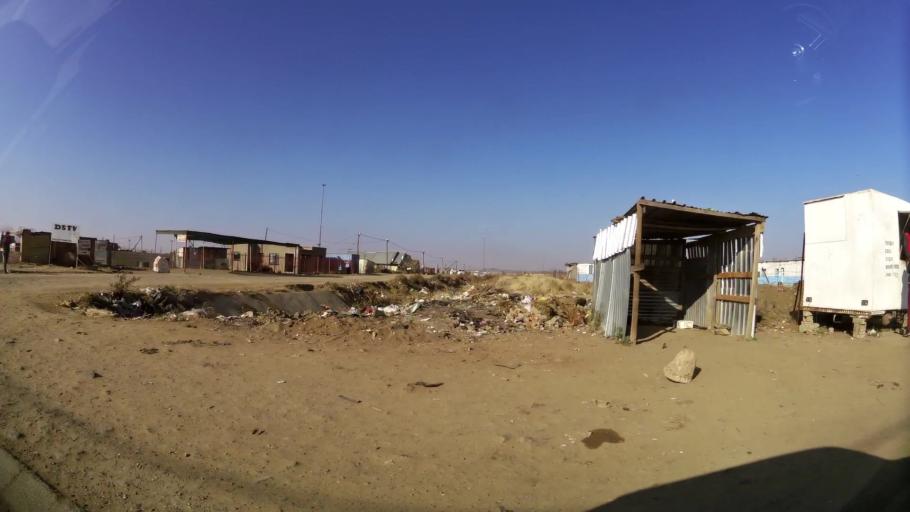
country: ZA
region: Orange Free State
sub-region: Mangaung Metropolitan Municipality
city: Bloemfontein
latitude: -29.2041
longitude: 26.2419
